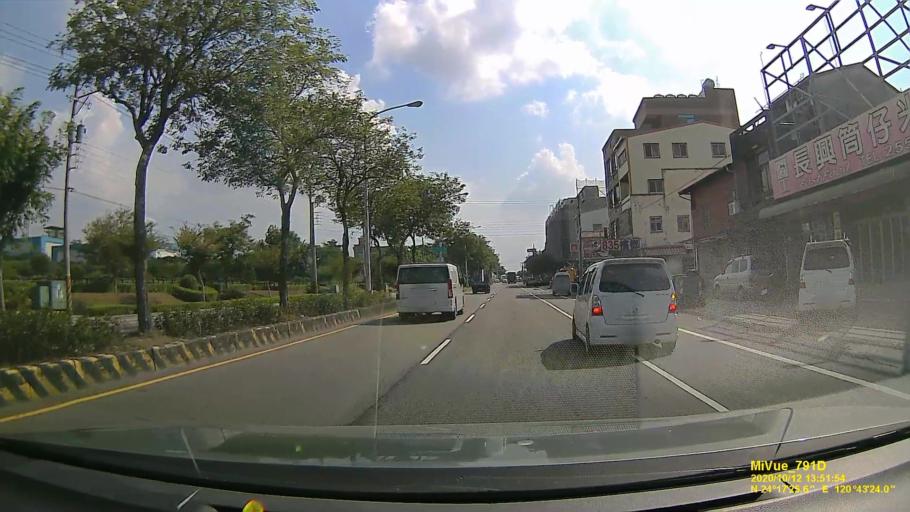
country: TW
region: Taiwan
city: Fengyuan
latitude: 24.2904
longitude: 120.7234
